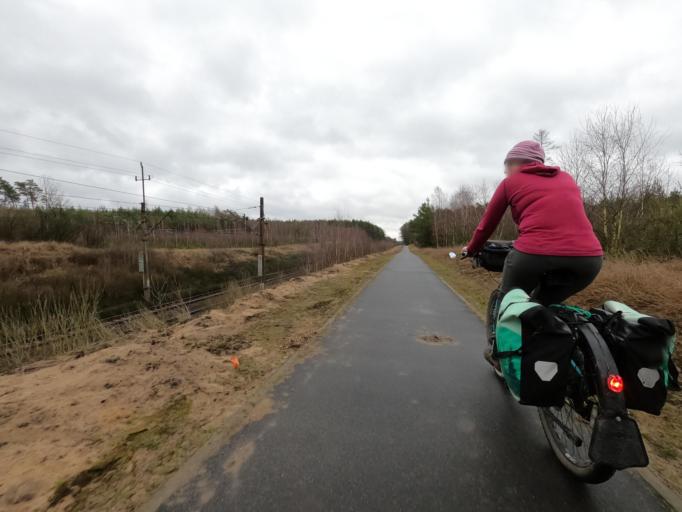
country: PL
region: Greater Poland Voivodeship
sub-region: Powiat pilski
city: Kaczory
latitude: 53.1218
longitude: 16.8220
